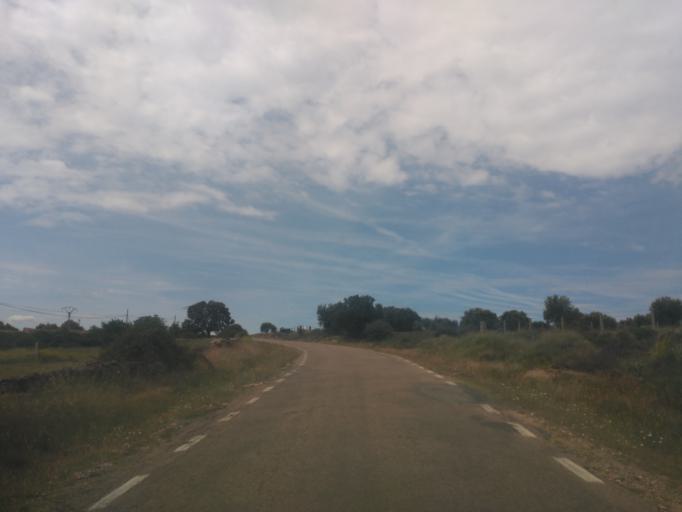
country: ES
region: Castille and Leon
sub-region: Provincia de Salamanca
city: Guijuelo
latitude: 40.5453
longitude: -5.6639
